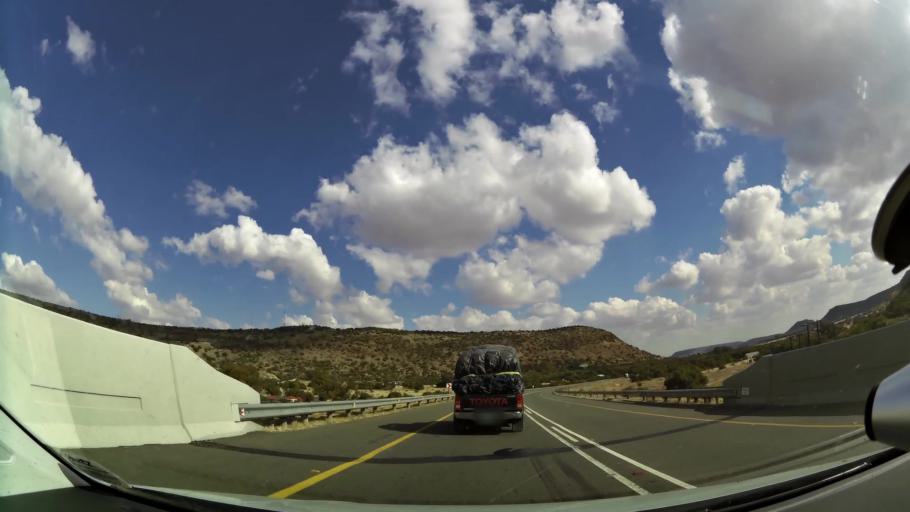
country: ZA
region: Orange Free State
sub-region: Mangaung Metropolitan Municipality
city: Bloemfontein
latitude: -29.1580
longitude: 26.0554
